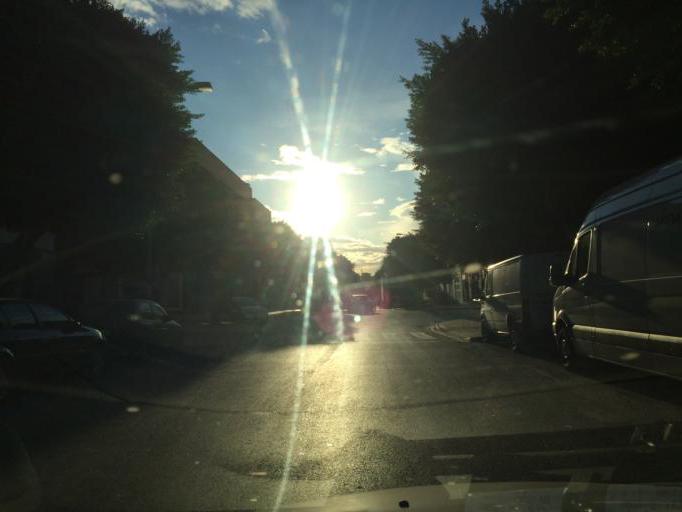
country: ES
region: Andalusia
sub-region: Provincia de Almeria
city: Almeria
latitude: 36.8367
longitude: -2.4440
